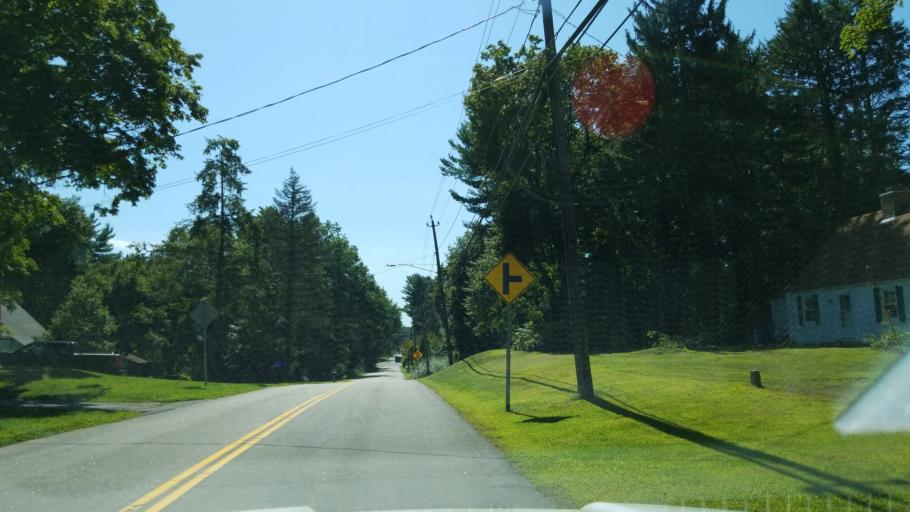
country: US
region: Connecticut
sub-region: Hartford County
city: Blue Hills
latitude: 41.8460
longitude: -72.7466
